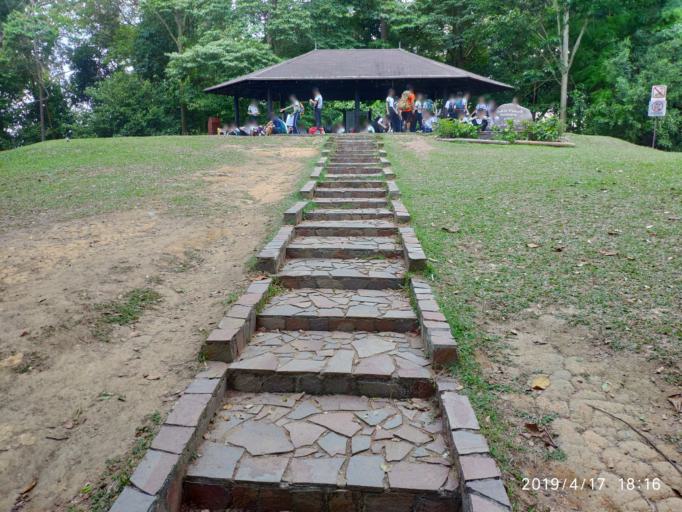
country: SG
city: Singapore
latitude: 1.3547
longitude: 103.7765
